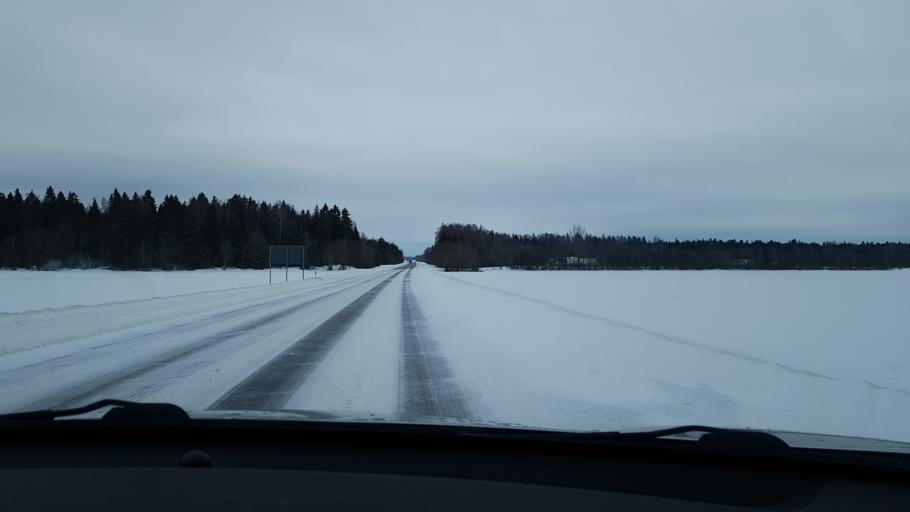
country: EE
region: Jaervamaa
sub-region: Jaerva-Jaani vald
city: Jarva-Jaani
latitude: 59.1373
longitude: 25.7724
